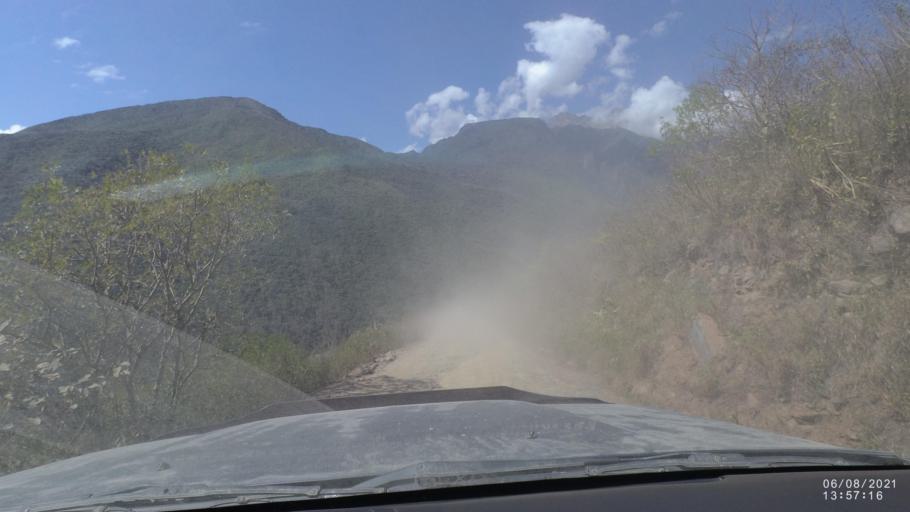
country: BO
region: La Paz
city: Quime
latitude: -16.6445
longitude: -66.7299
